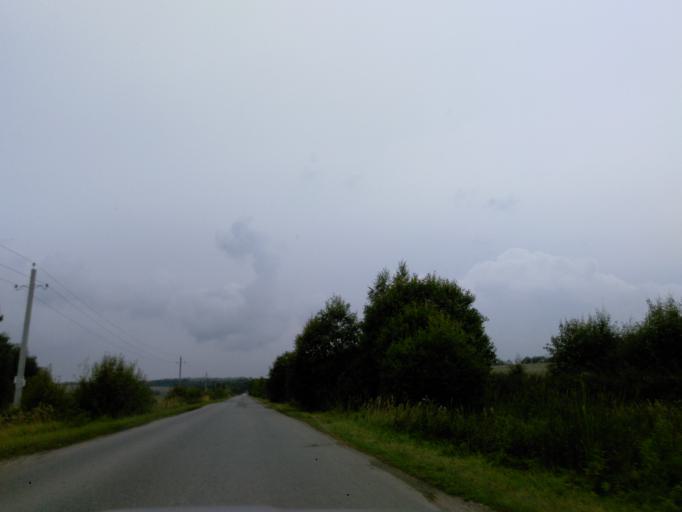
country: RU
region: Moskovskaya
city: Mendeleyevo
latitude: 56.1107
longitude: 37.2361
